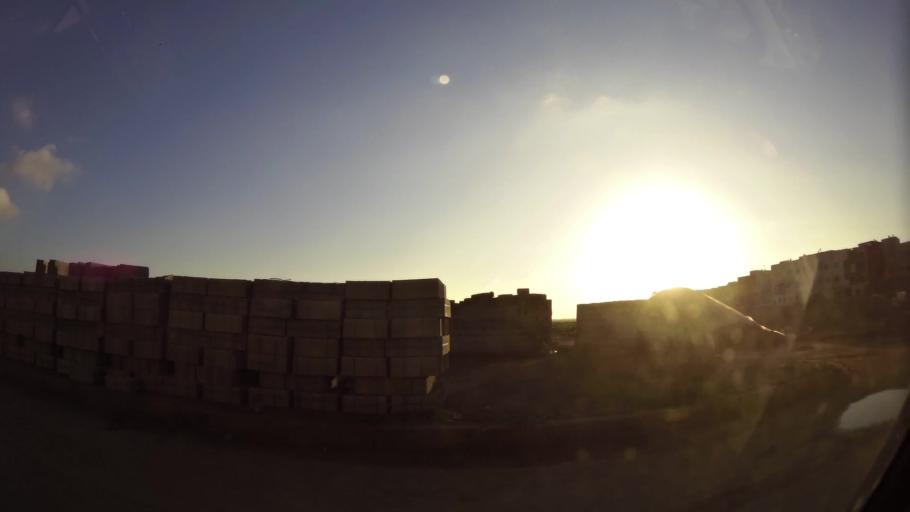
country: MA
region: Chaouia-Ouardigha
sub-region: Settat Province
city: Settat
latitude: 32.9850
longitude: -7.5994
